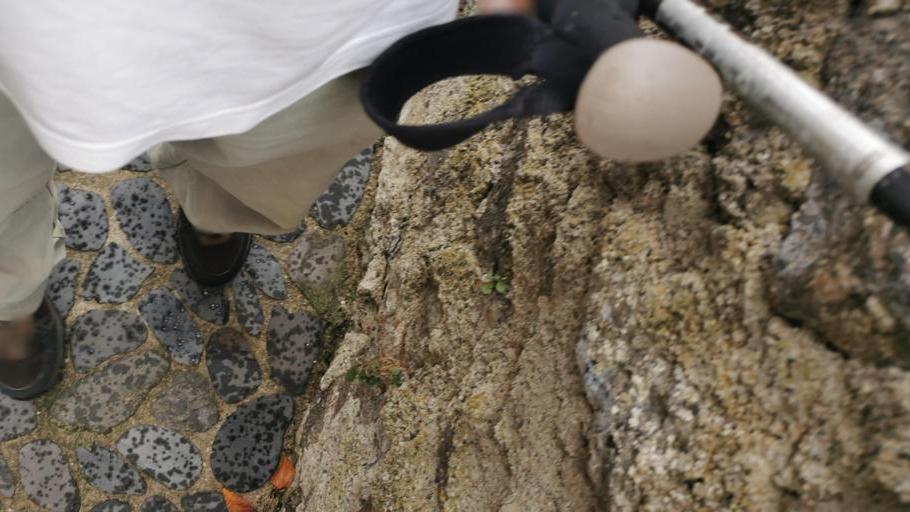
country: FR
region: Auvergne
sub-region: Departement de la Haute-Loire
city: Polignac
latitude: 45.0713
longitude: 3.8601
